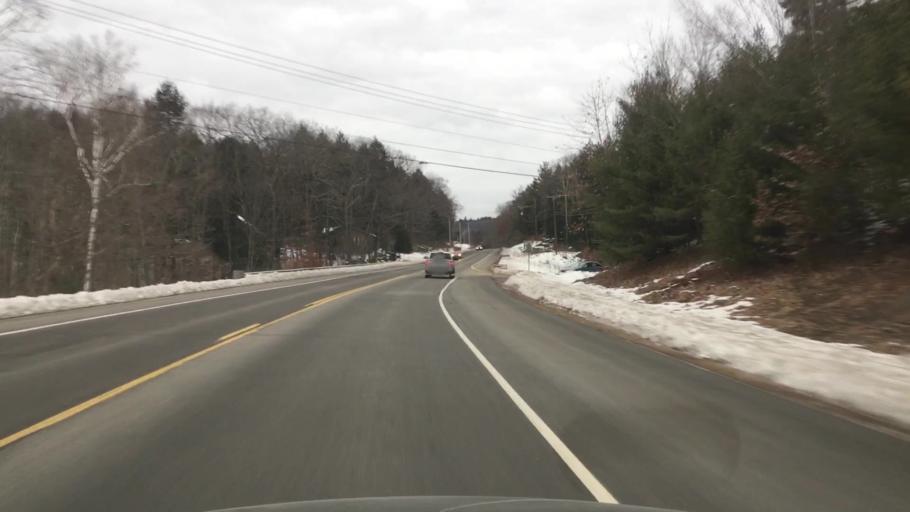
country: US
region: New Hampshire
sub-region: Merrimack County
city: Newbury
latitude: 43.3044
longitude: -72.0110
